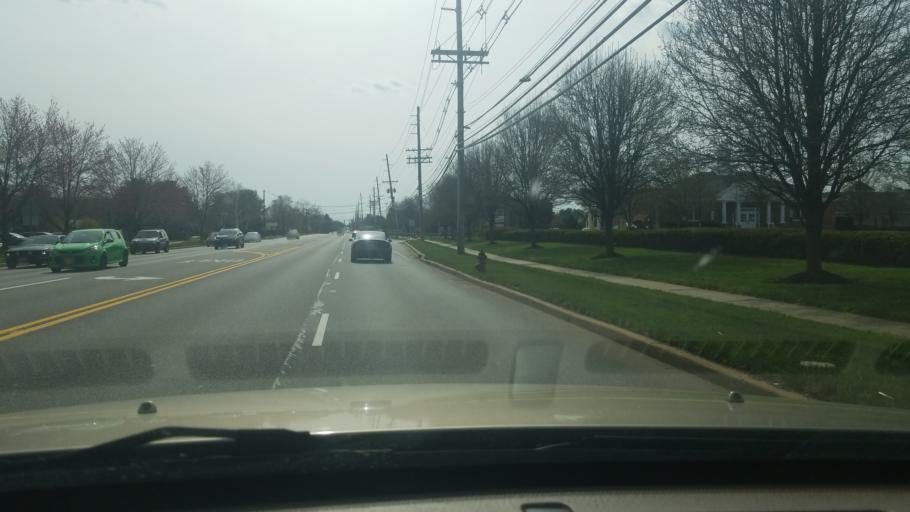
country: US
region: New Jersey
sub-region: Monmouth County
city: West Freehold
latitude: 40.2417
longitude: -74.3026
